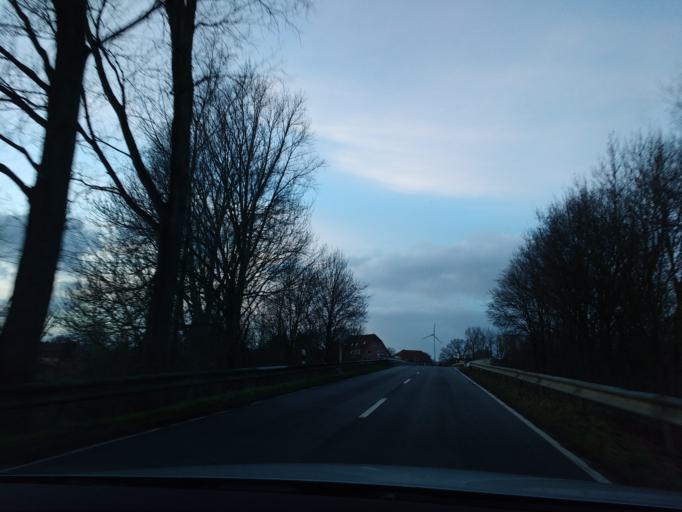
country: DE
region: Lower Saxony
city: Schwarmstedt
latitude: 52.6411
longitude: 9.5814
